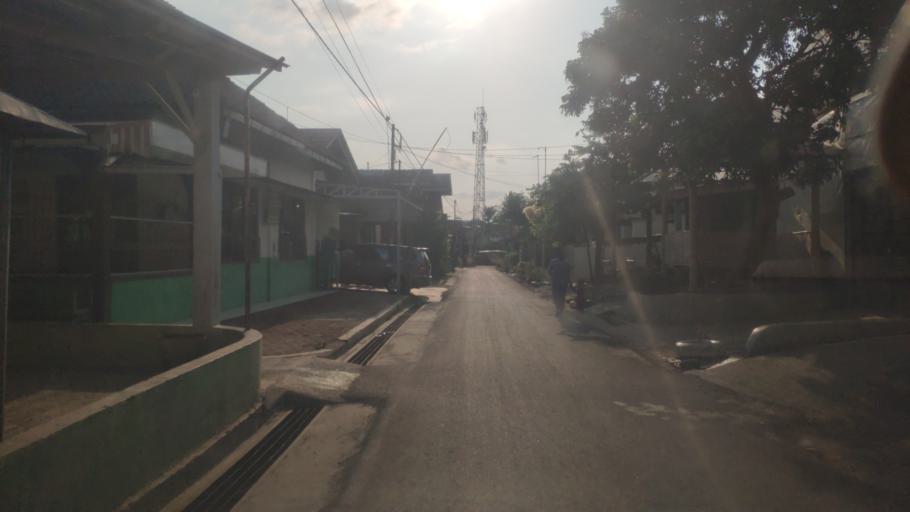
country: ID
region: Central Java
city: Wonosobo
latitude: -7.3993
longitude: 109.6941
